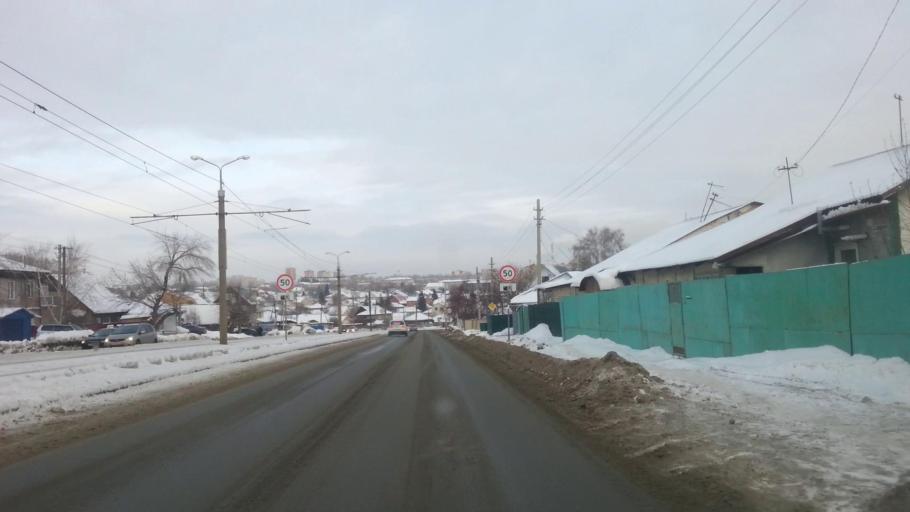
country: RU
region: Altai Krai
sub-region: Gorod Barnaulskiy
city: Barnaul
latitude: 53.3646
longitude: 83.7302
